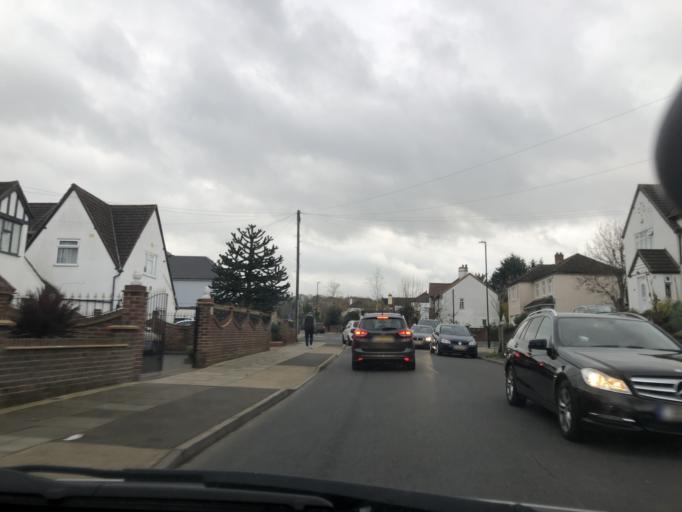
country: GB
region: England
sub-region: Greater London
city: Bexley
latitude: 51.4341
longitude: 0.1659
